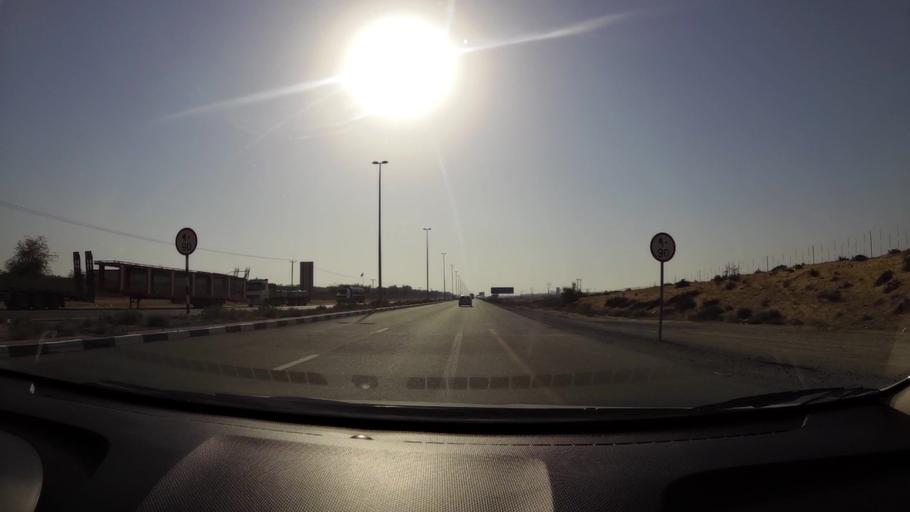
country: AE
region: Umm al Qaywayn
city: Umm al Qaywayn
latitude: 25.4298
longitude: 55.5823
